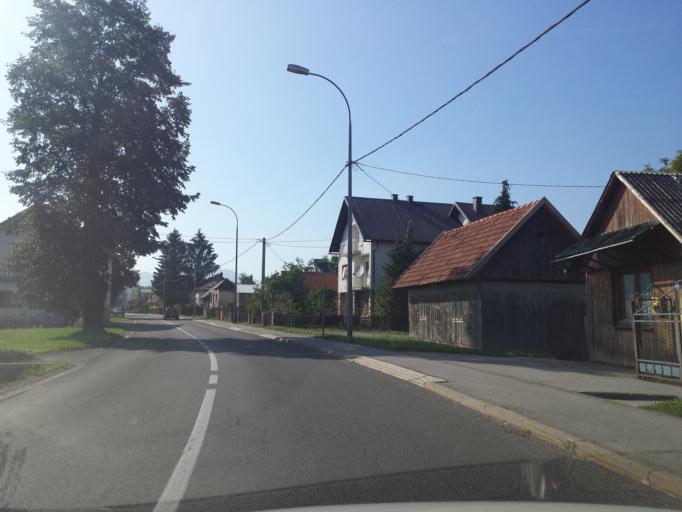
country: HR
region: Karlovacka
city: Ostarije
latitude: 45.2265
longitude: 15.2733
